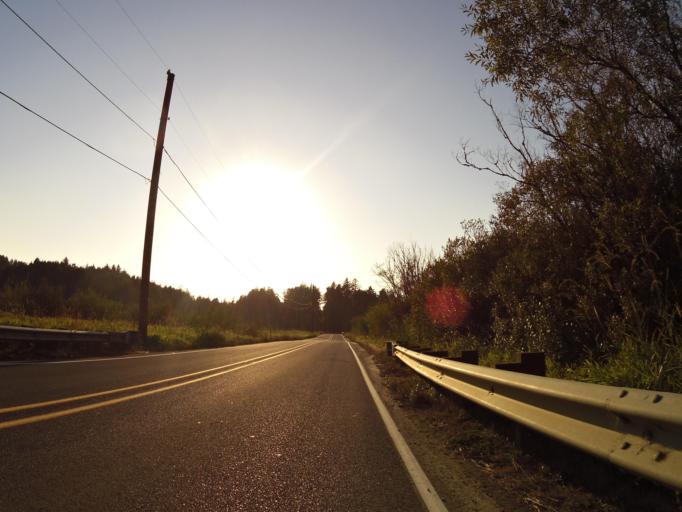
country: US
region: Oregon
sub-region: Lincoln County
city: Lincoln City
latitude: 44.9616
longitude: -124.0005
